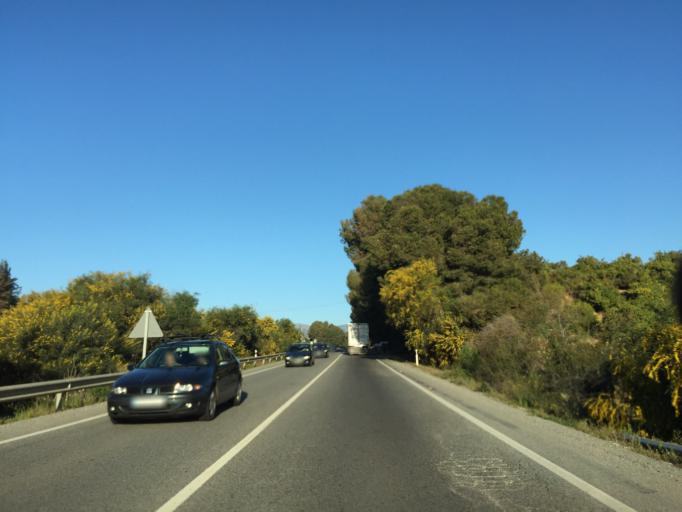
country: ES
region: Andalusia
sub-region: Provincia de Malaga
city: Pizarra
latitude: 36.7477
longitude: -4.7133
